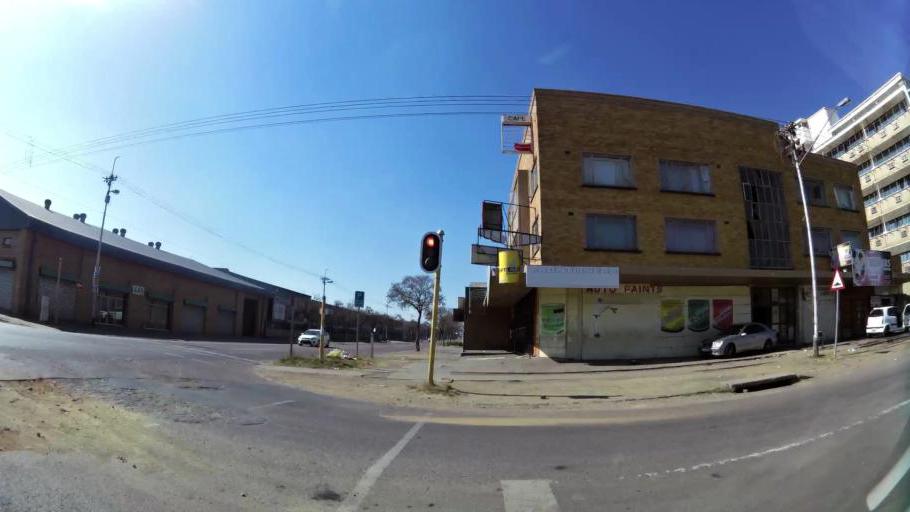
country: ZA
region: Gauteng
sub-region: City of Tshwane Metropolitan Municipality
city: Pretoria
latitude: -25.7553
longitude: 28.1553
